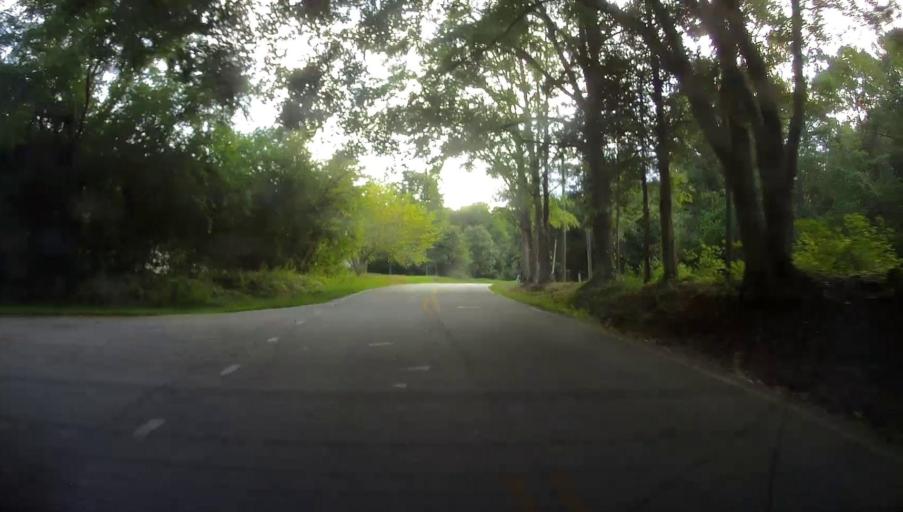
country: US
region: Georgia
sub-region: Monroe County
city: Forsyth
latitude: 33.0151
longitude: -83.9619
